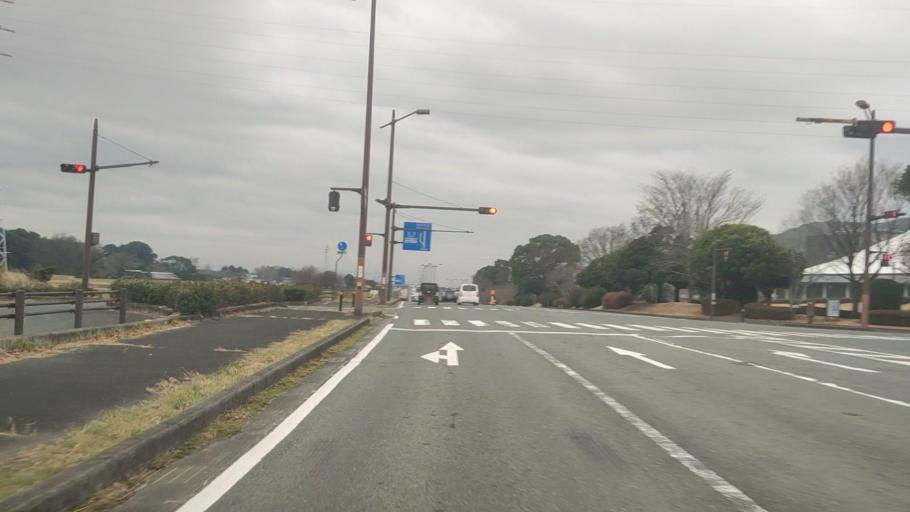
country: JP
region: Kumamoto
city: Ozu
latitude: 32.8396
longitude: 130.8053
